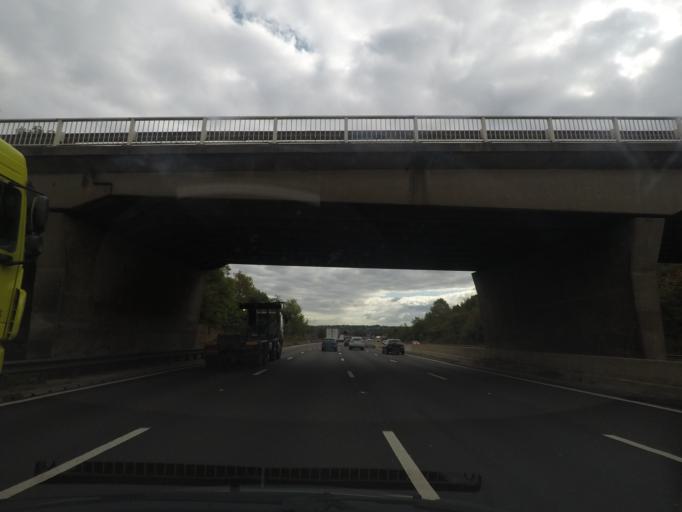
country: GB
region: England
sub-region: Sheffield
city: Chapletown
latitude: 53.4554
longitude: -1.4451
